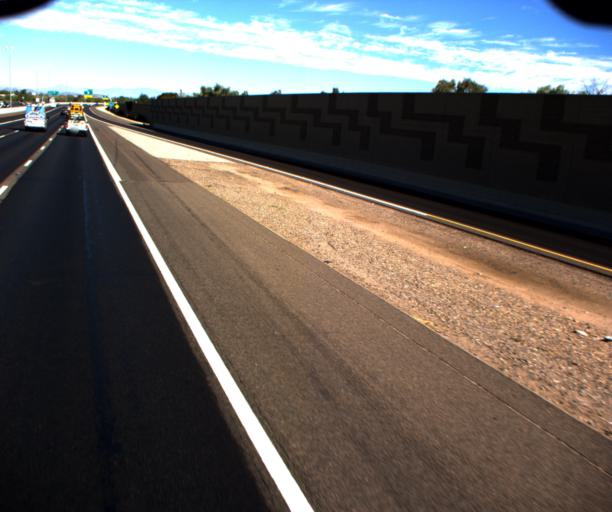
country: US
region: Arizona
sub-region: Maricopa County
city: Sun City
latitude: 33.5834
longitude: -112.2599
